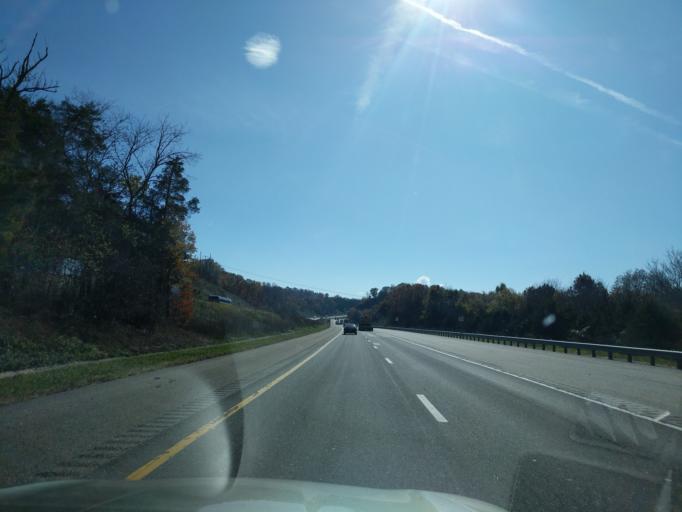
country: US
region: Virginia
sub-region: Rockbridge County
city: East Lexington
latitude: 37.7854
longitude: -79.4006
